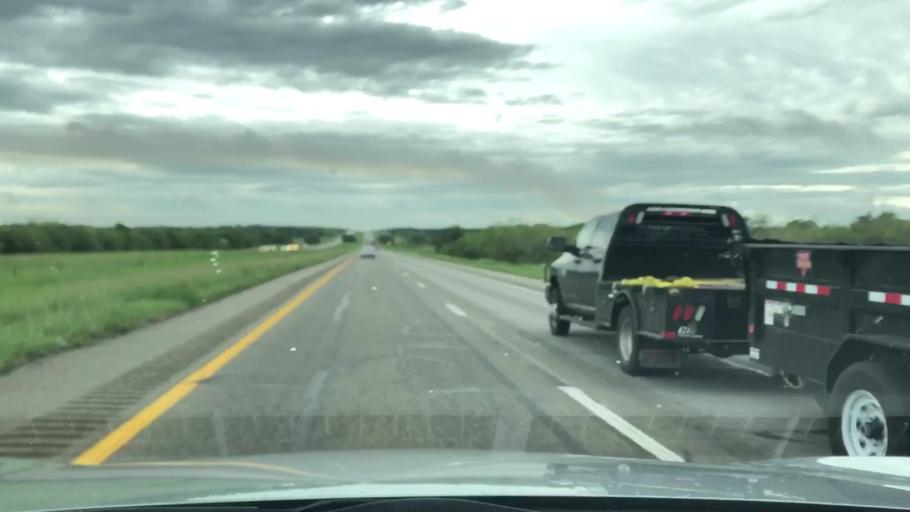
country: US
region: Texas
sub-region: Caldwell County
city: Luling
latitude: 29.6361
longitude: -97.7301
